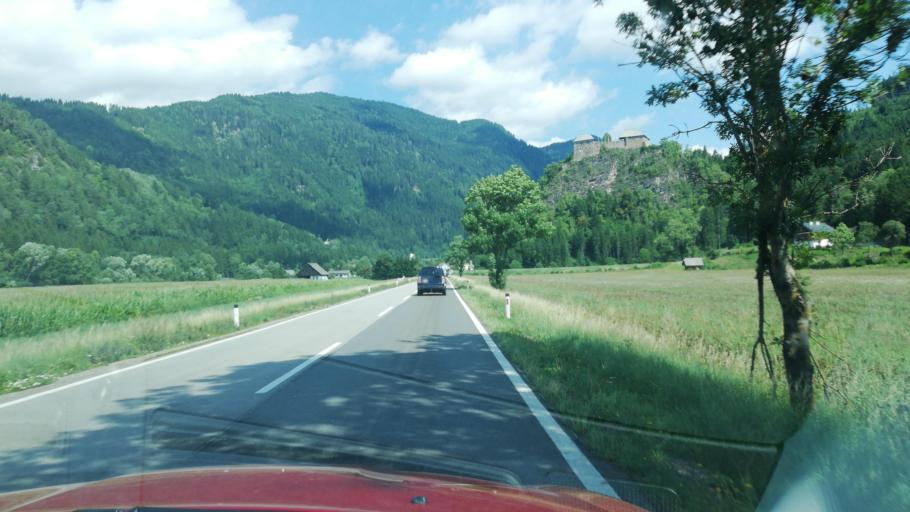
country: AT
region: Styria
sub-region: Politischer Bezirk Murau
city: Durnstein in der Steiermark
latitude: 46.9848
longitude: 14.3909
